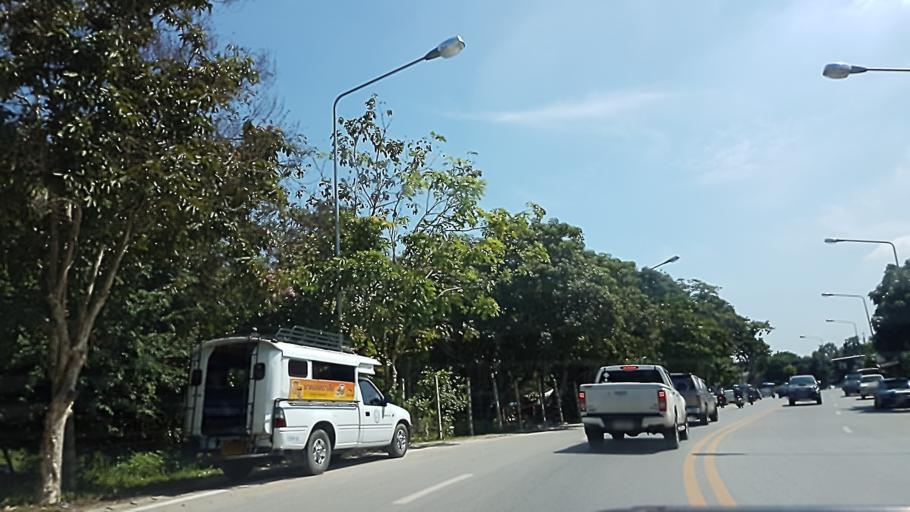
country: TH
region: Chiang Mai
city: Chiang Mai
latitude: 18.8217
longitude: 98.9697
